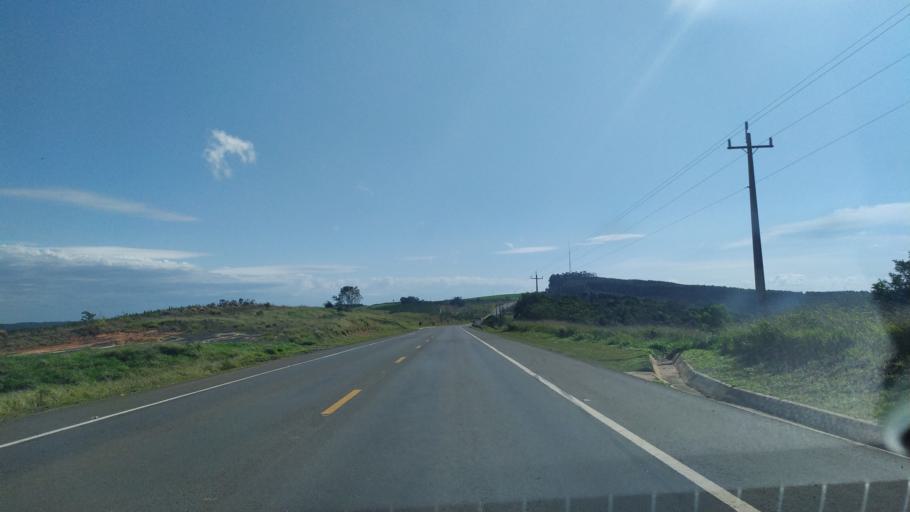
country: BR
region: Parana
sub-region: Ortigueira
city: Ortigueira
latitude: -24.2930
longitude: -50.8282
